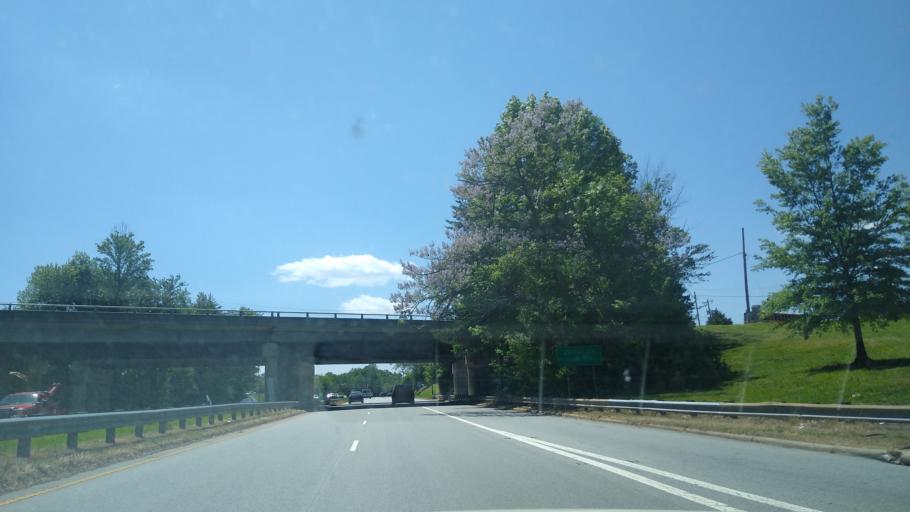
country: US
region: North Carolina
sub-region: Guilford County
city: Greensboro
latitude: 36.0622
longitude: -79.8598
